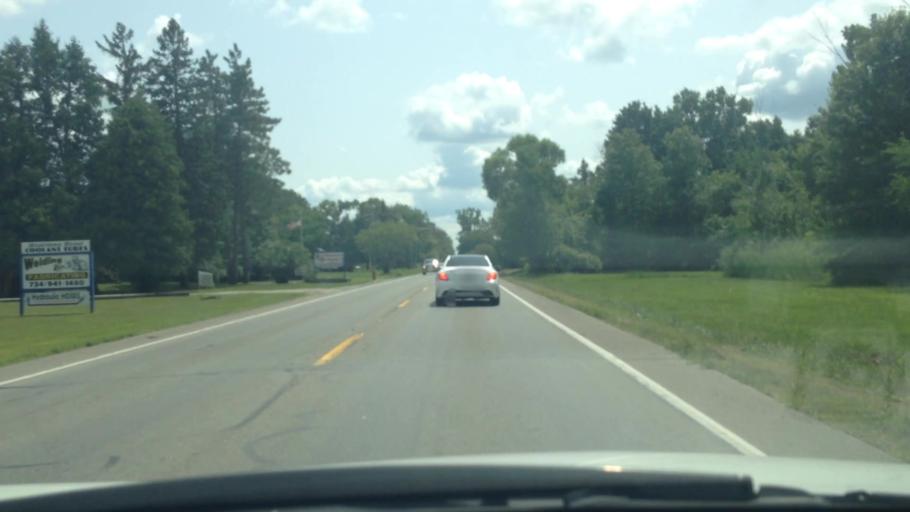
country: US
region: Michigan
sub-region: Wayne County
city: Taylor
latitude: 42.2194
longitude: -83.3074
